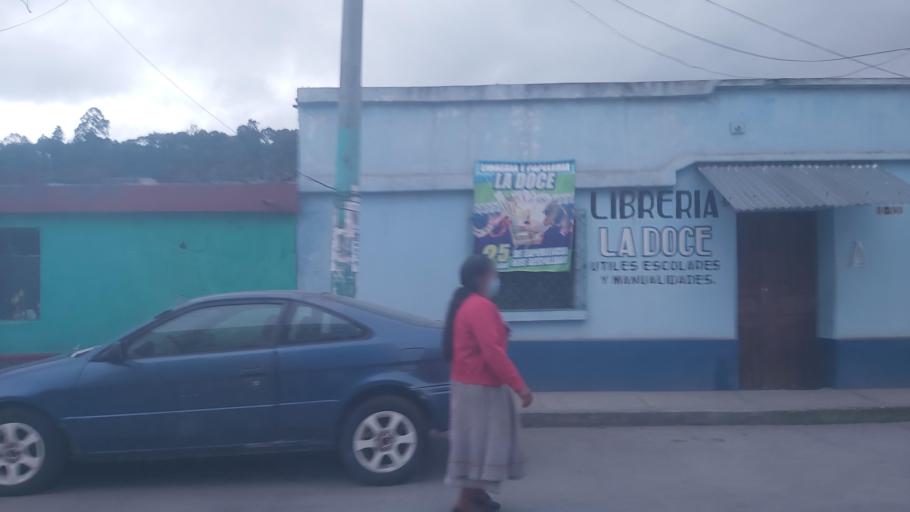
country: GT
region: Quetzaltenango
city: Quetzaltenango
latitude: 14.8300
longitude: -91.5283
